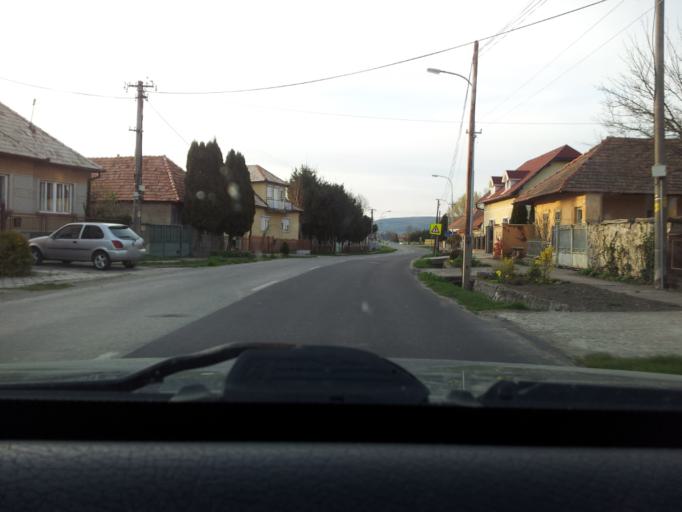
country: SK
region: Nitriansky
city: Levice
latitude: 48.2571
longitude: 18.6049
